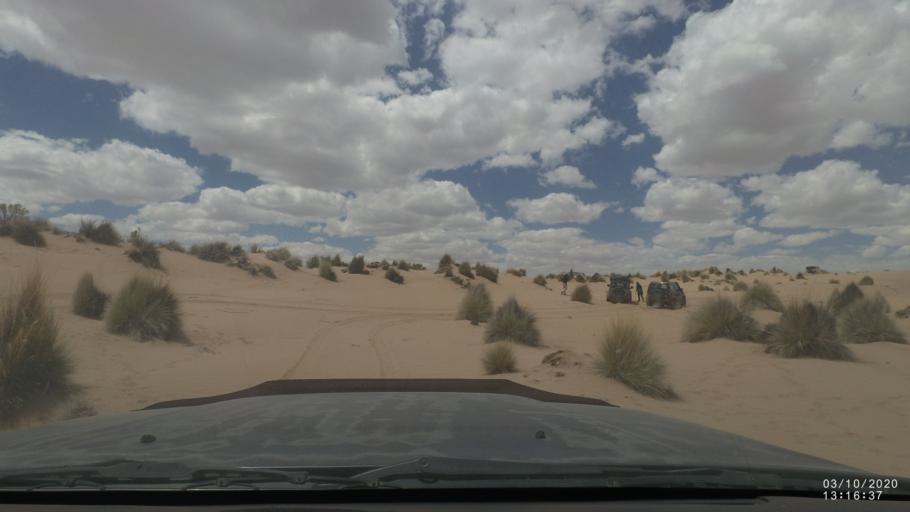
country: BO
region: Oruro
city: Poopo
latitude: -18.6909
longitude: -67.5335
